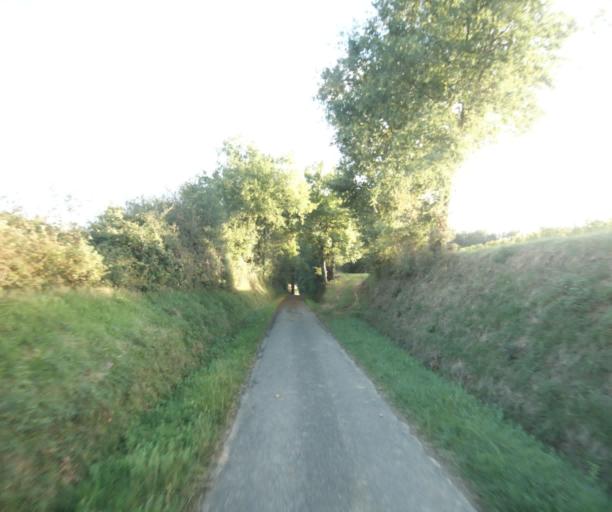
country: FR
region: Midi-Pyrenees
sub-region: Departement du Gers
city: Le Houga
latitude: 43.8315
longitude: -0.1099
